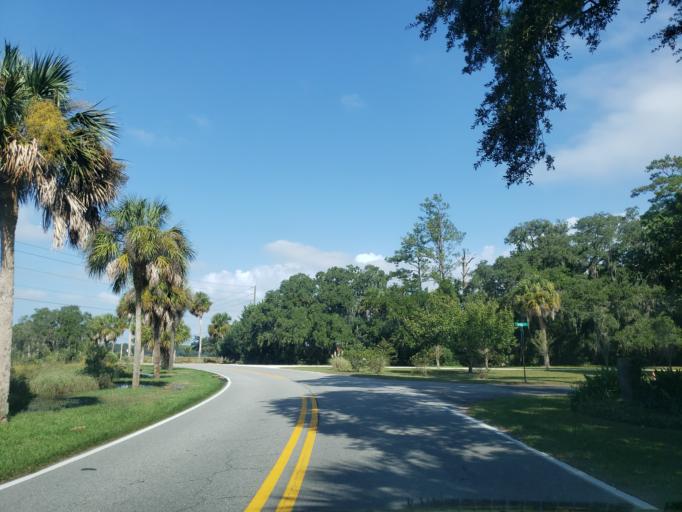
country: US
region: Georgia
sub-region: Chatham County
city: Montgomery
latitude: 31.9321
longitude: -81.0978
